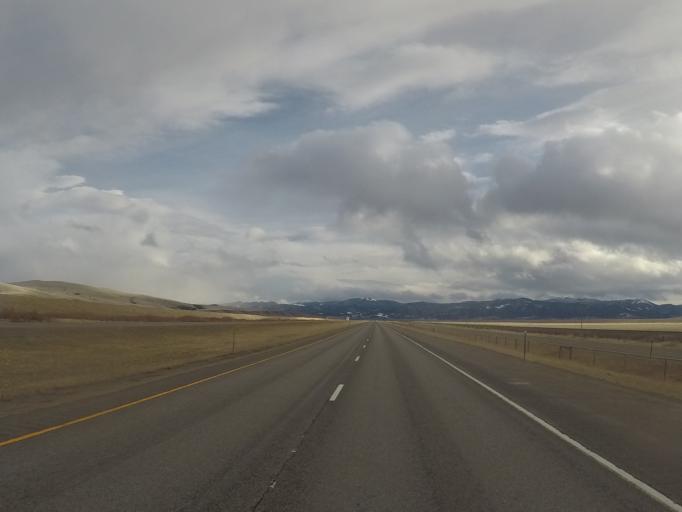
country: US
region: Montana
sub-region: Deer Lodge County
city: Warm Springs
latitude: 46.1638
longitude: -112.7910
